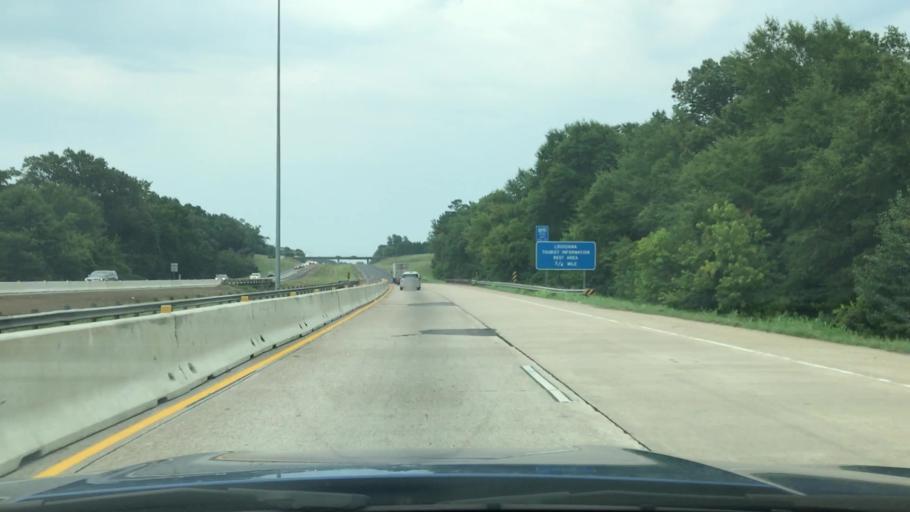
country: US
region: Louisiana
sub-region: Caddo Parish
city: Greenwood
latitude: 32.4517
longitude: -94.0190
